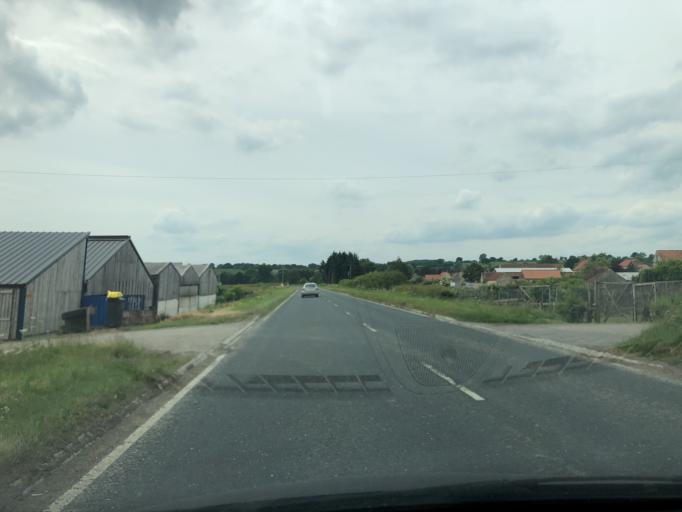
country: GB
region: England
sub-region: North Yorkshire
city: Pickering
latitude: 54.2629
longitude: -0.8215
